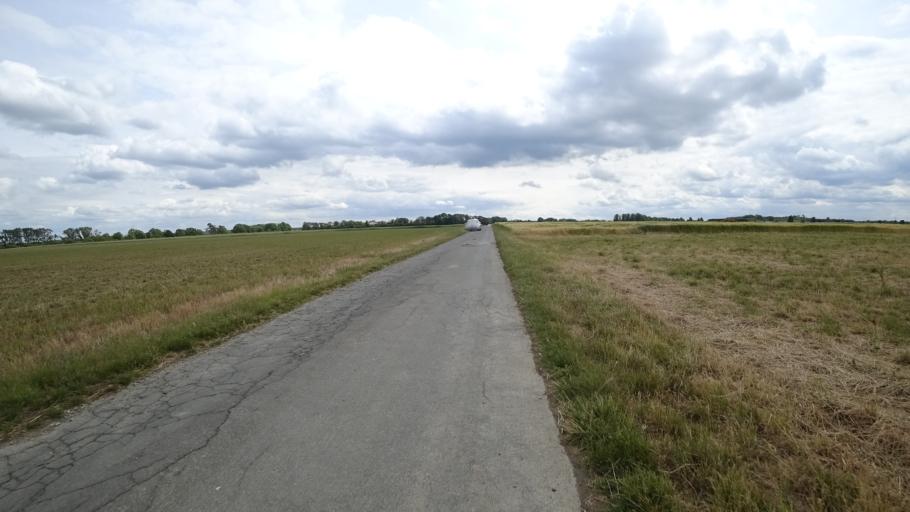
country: DE
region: North Rhine-Westphalia
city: Erwitte
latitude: 51.6109
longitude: 8.3937
